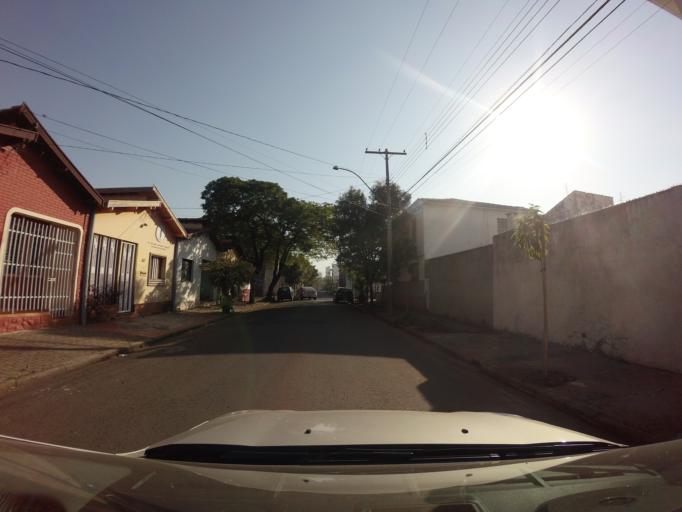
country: BR
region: Sao Paulo
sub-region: Piracicaba
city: Piracicaba
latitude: -22.7345
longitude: -47.6464
